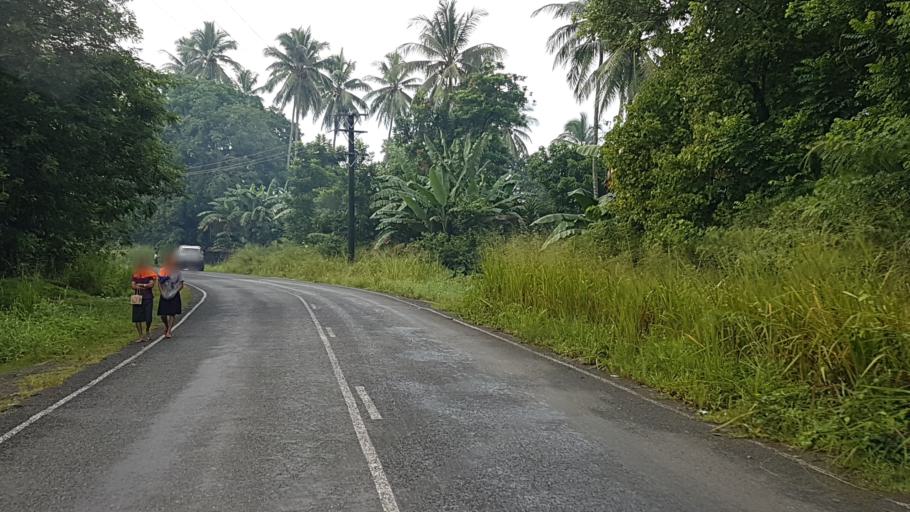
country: PG
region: Milne Bay
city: Alotau
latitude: -10.3222
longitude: 150.4778
